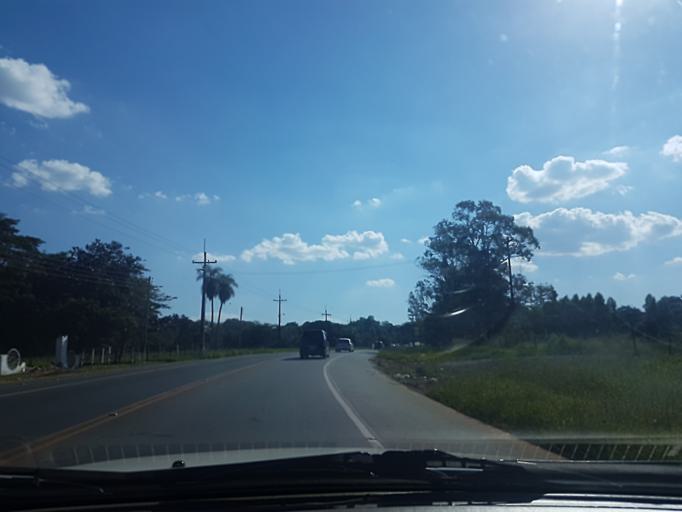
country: PY
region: Central
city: Aregua
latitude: -25.2377
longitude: -57.4225
